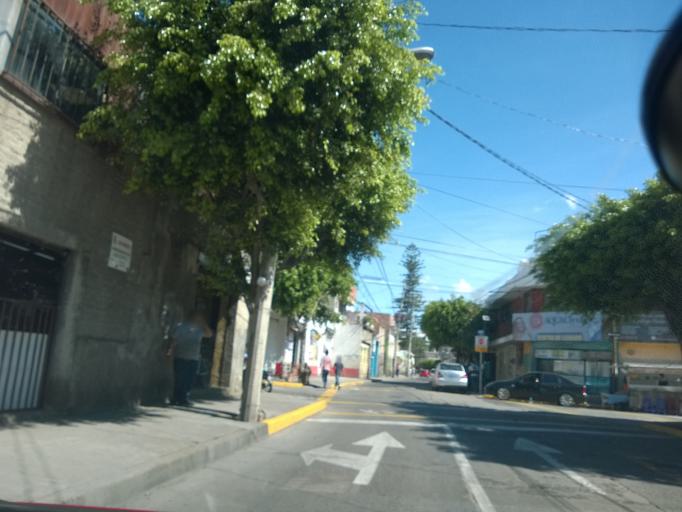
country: MX
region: Guanajuato
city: Leon
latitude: 21.1158
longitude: -101.6783
